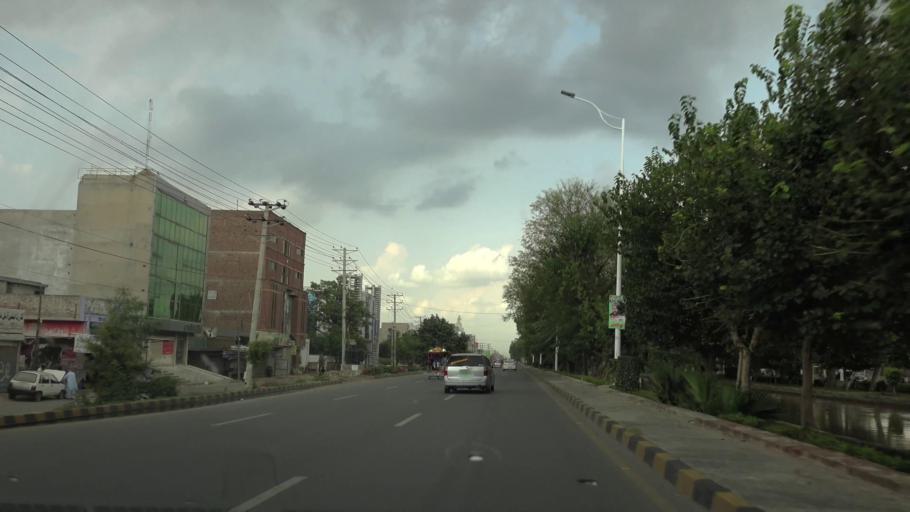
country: PK
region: Punjab
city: Faisalabad
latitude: 31.4362
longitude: 73.1281
